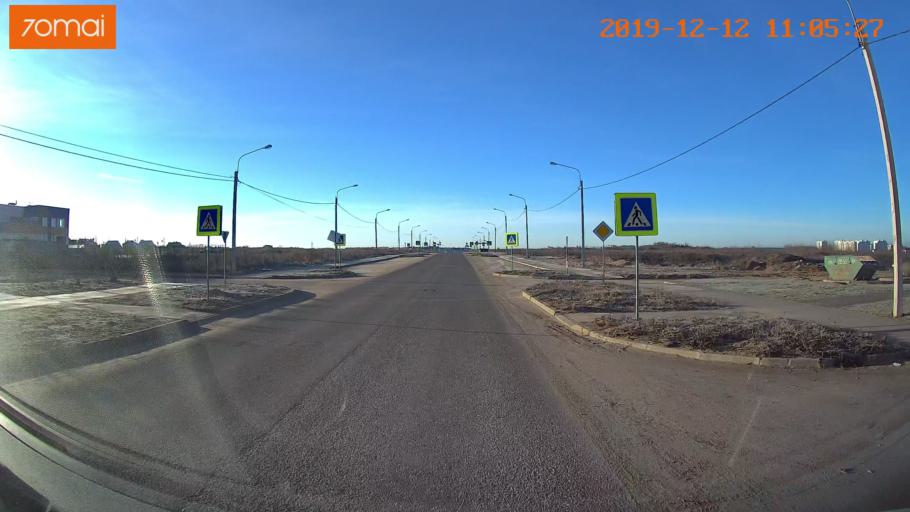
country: RU
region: Ivanovo
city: Kokhma
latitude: 56.9492
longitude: 41.0987
